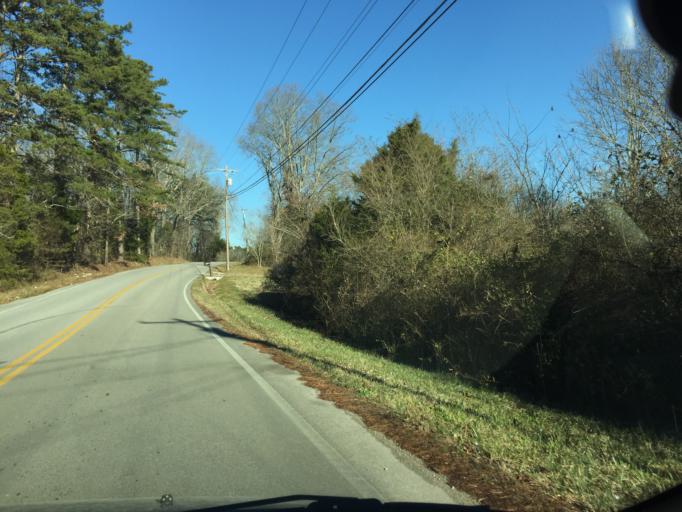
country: US
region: Tennessee
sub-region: Hamilton County
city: Collegedale
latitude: 35.0613
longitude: -85.0961
